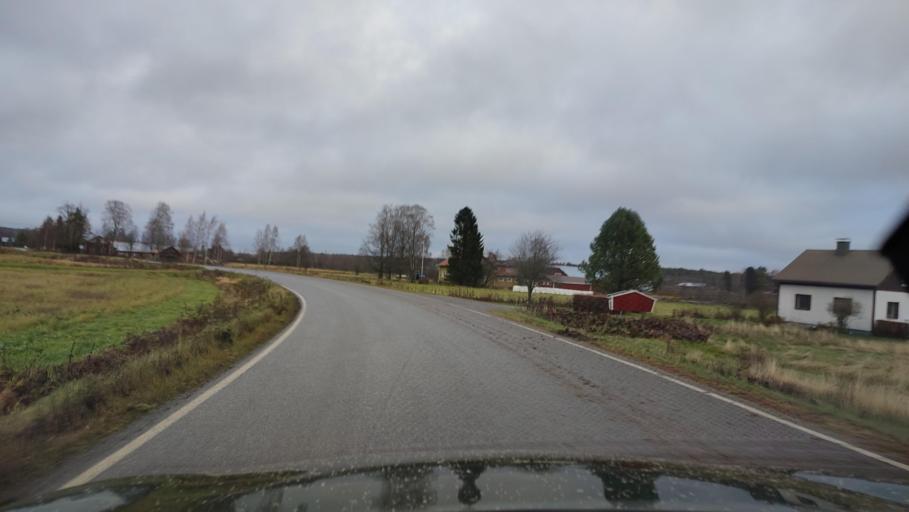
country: FI
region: Southern Ostrobothnia
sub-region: Suupohja
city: Karijoki
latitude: 62.3903
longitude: 21.5595
